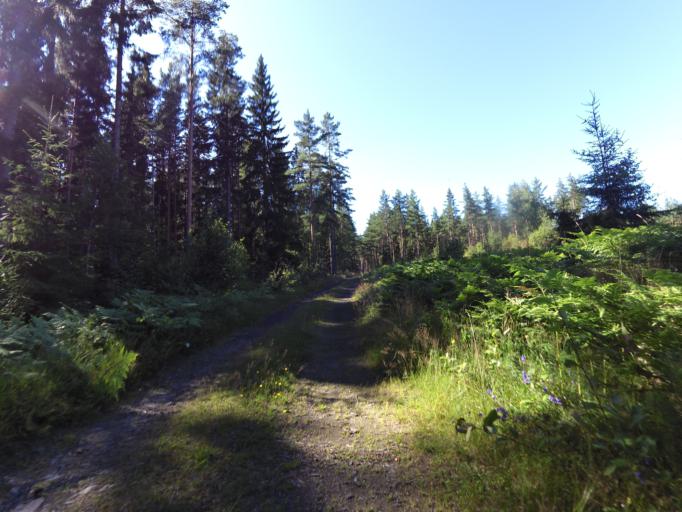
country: SE
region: Gaevleborg
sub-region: Hofors Kommun
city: Hofors
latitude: 60.5743
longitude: 16.4390
